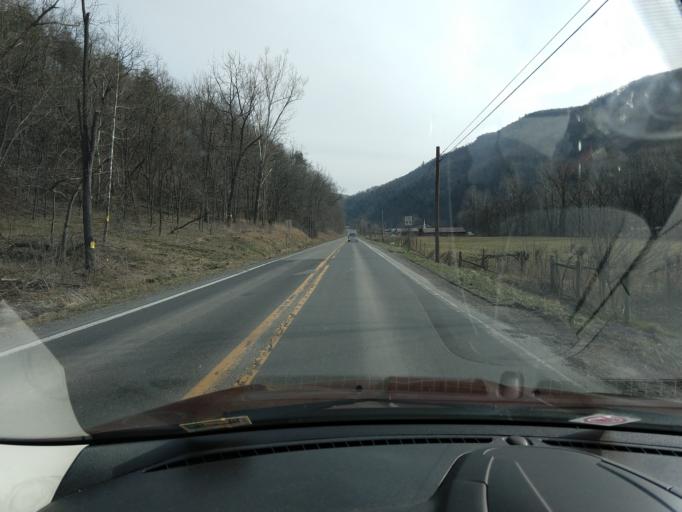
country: US
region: West Virginia
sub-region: Pendleton County
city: Franklin
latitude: 38.7921
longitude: -79.4051
